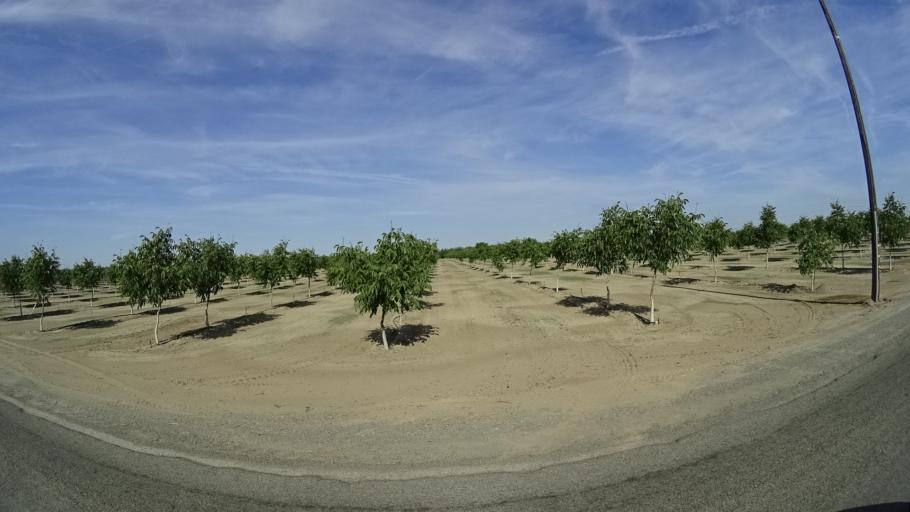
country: US
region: California
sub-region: Tulare County
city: Goshen
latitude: 36.3407
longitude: -119.4930
